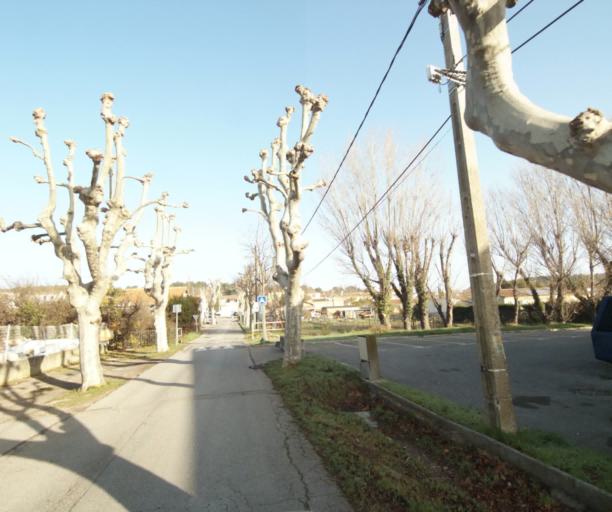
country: FR
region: Provence-Alpes-Cote d'Azur
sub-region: Departement des Bouches-du-Rhone
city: Septemes-les-Vallons
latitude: 43.4170
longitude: 5.3543
